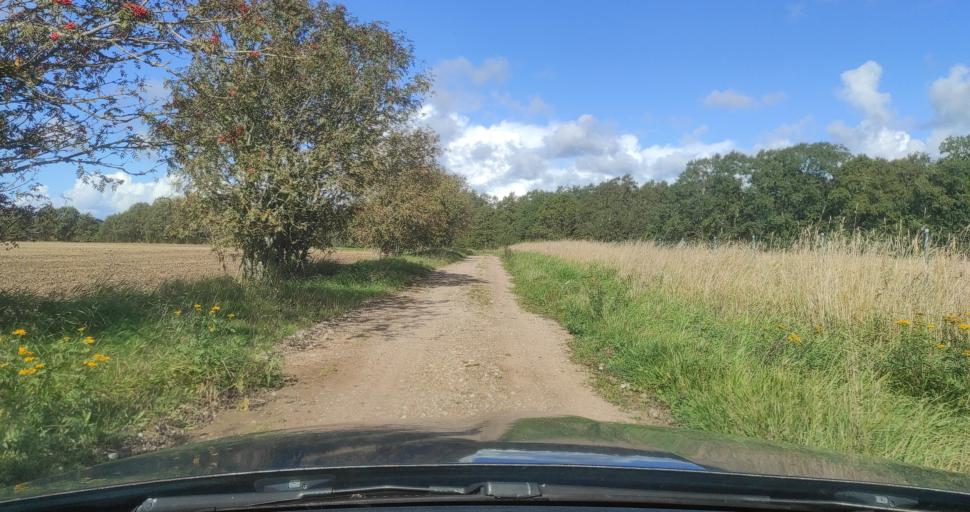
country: LV
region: Ventspils Rajons
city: Piltene
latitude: 57.2678
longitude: 21.6052
